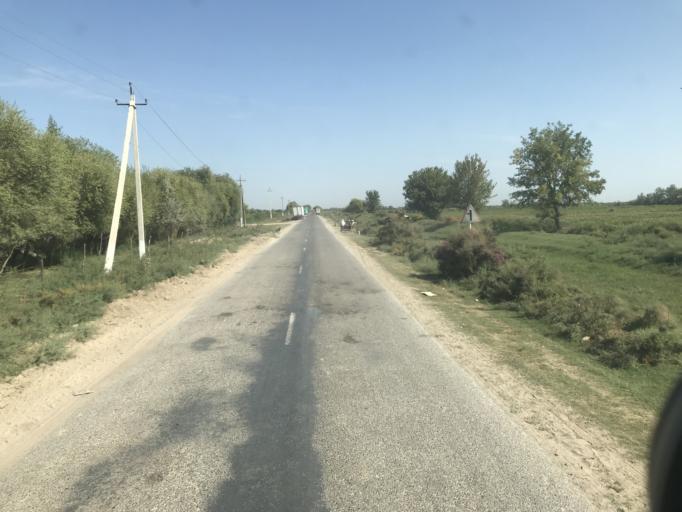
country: KZ
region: Ongtustik Qazaqstan
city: Myrzakent
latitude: 40.6662
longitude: 68.6332
